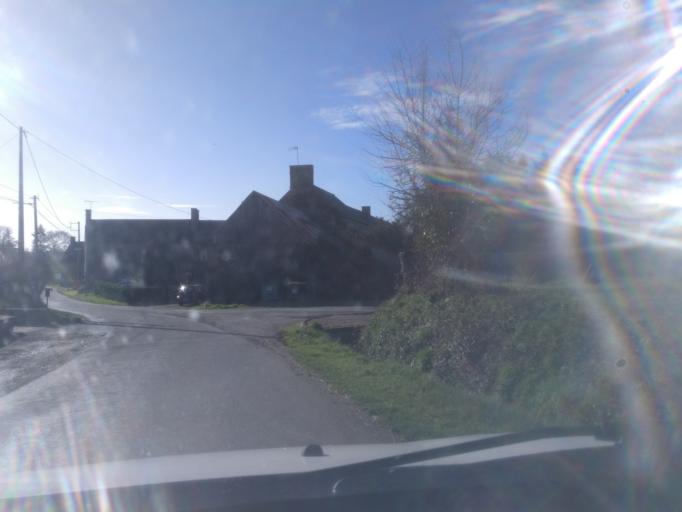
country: FR
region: Lower Normandy
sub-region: Departement de la Manche
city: Pontorson
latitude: 48.5241
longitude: -1.5227
